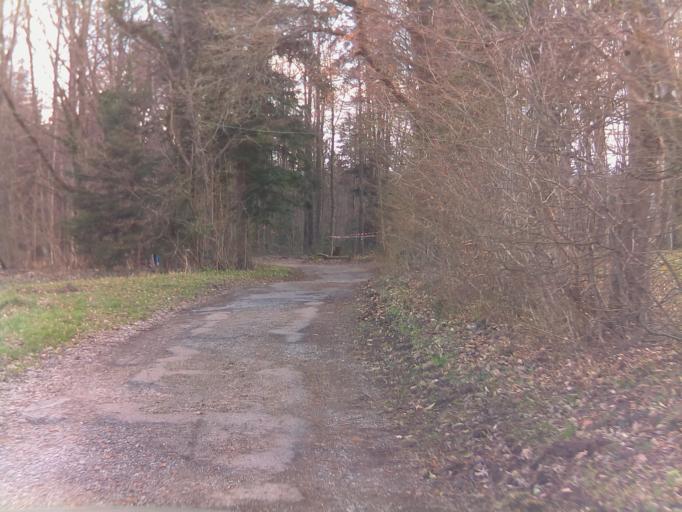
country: DE
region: Baden-Wuerttemberg
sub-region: Regierungsbezirk Stuttgart
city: Althutte
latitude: 48.8980
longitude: 9.6022
